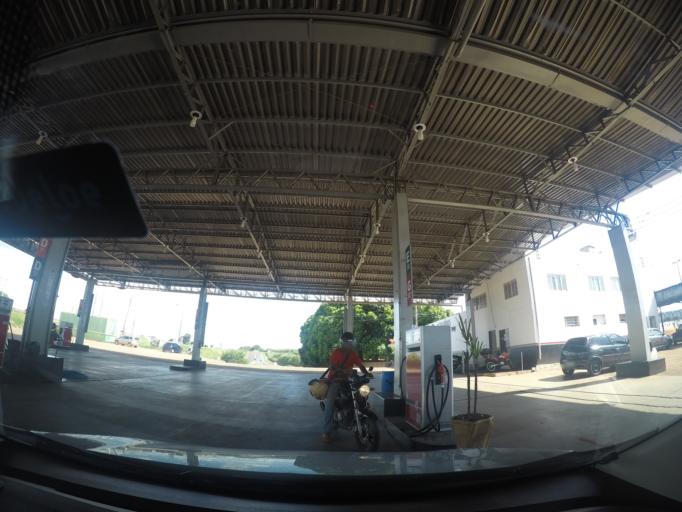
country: BR
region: Sao Paulo
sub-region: Barretos
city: Barretos
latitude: -20.5436
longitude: -48.5946
